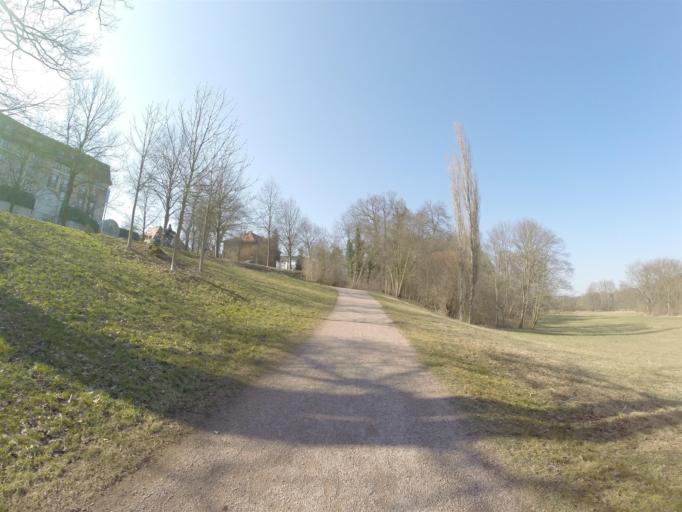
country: DE
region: Thuringia
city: Weimar
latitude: 50.9678
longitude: 11.3372
